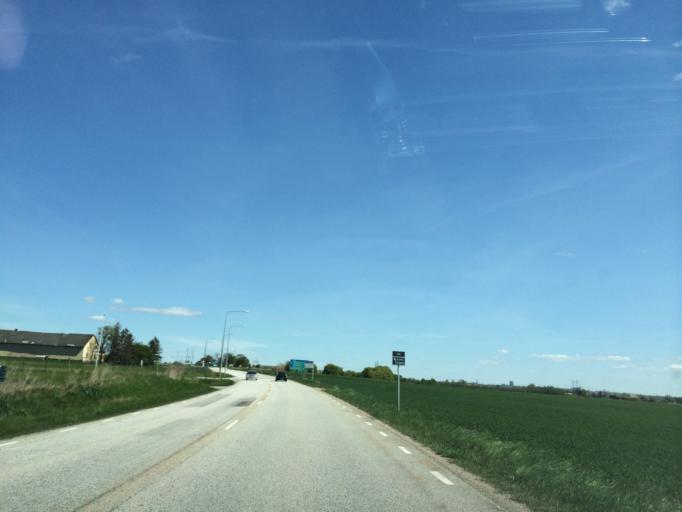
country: SE
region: Skane
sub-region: Lomma Kommun
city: Lomma
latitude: 55.7204
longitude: 13.0832
